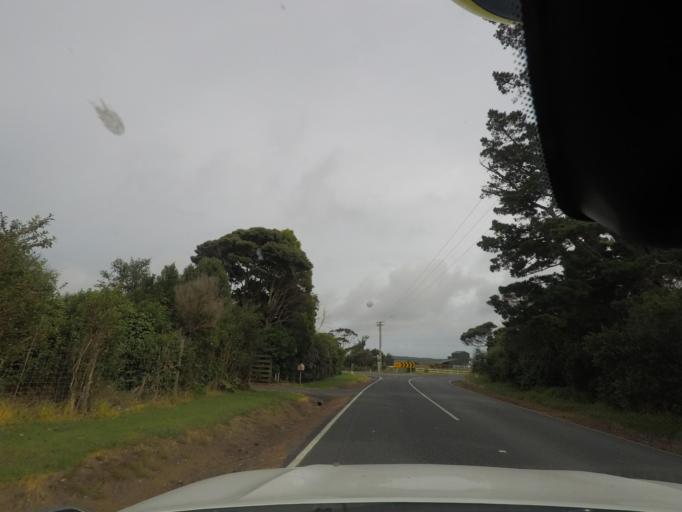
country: NZ
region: Auckland
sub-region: Auckland
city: Parakai
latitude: -36.4869
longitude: 174.2471
